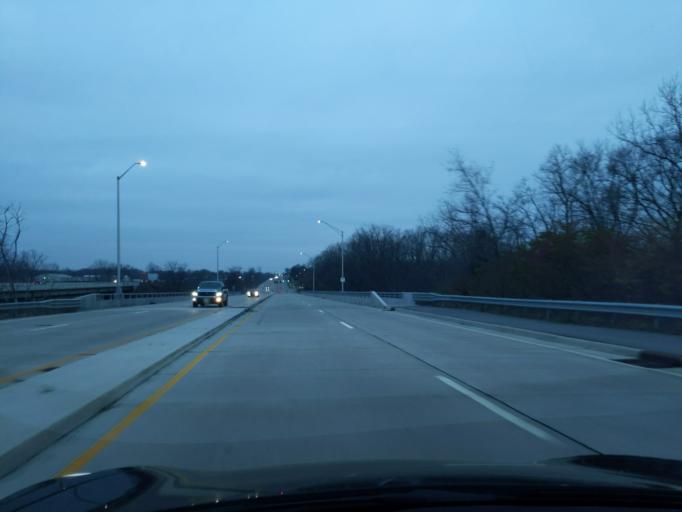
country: US
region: Indiana
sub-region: Saint Joseph County
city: Notre Dame
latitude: 41.7231
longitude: -86.2659
